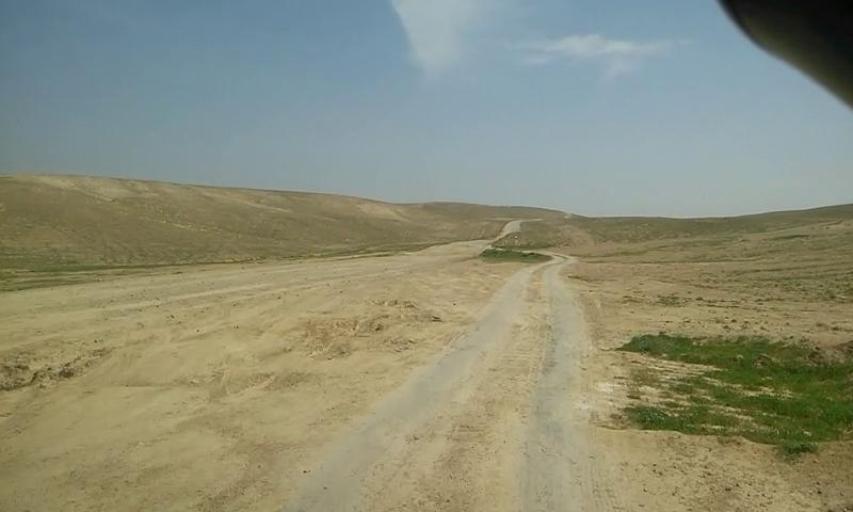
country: PS
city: `Arab ar Rashaydah
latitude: 31.5290
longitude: 35.2901
